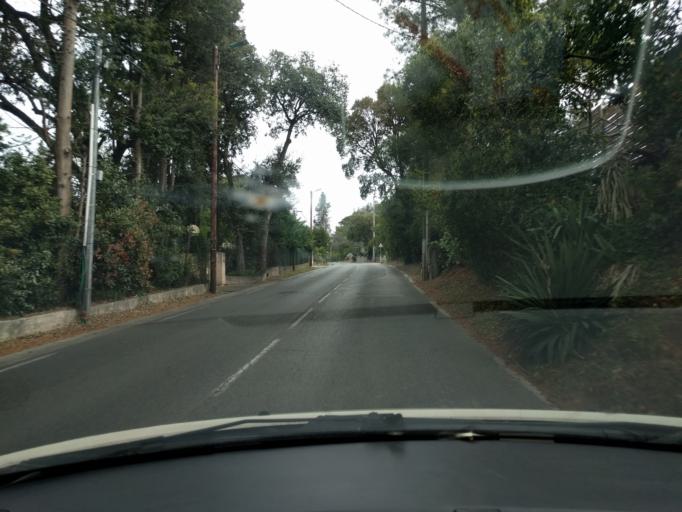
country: FR
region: Provence-Alpes-Cote d'Azur
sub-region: Departement des Alpes-Maritimes
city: La Roquette-sur-Siagne
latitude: 43.5855
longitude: 6.9569
